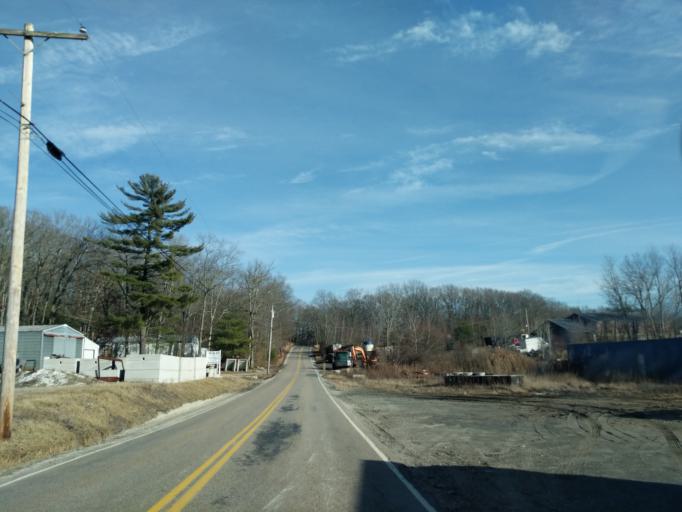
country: US
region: Massachusetts
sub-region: Worcester County
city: Millville
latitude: 42.0270
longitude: -71.5659
